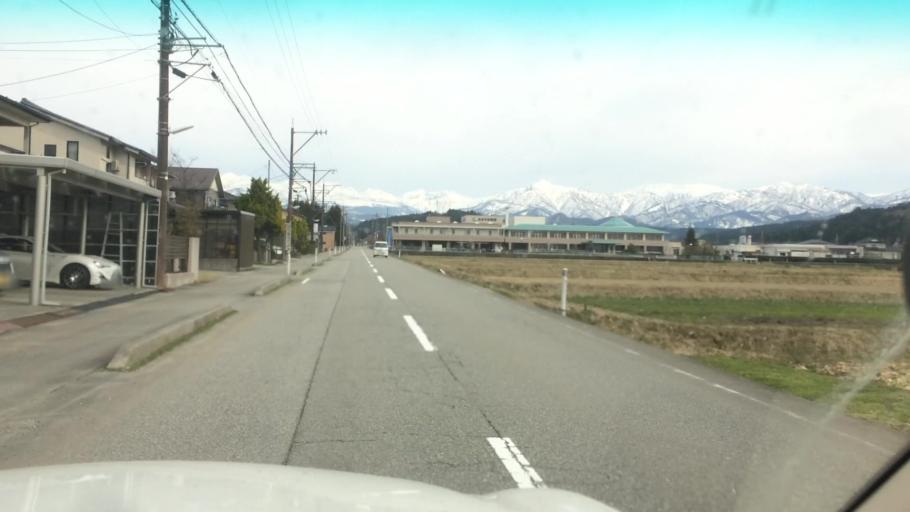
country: JP
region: Toyama
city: Toyama-shi
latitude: 36.6109
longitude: 137.2769
